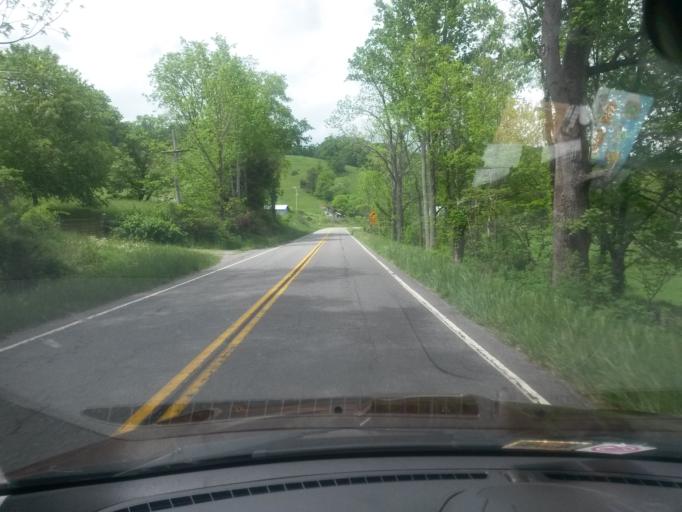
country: US
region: Virginia
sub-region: Floyd County
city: Floyd
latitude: 36.8805
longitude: -80.3298
